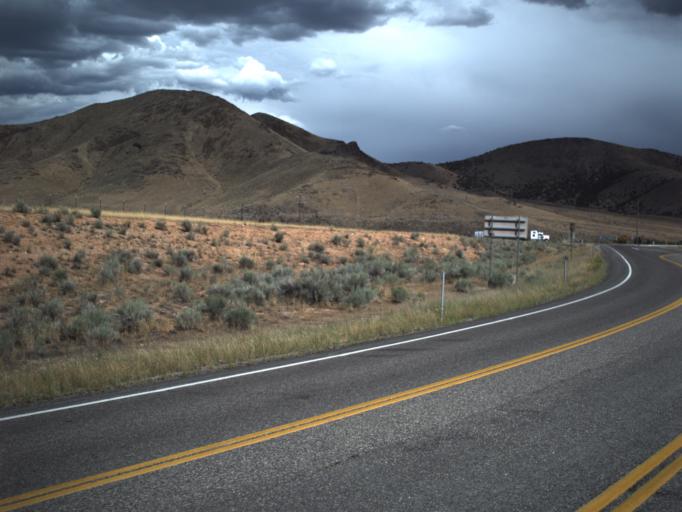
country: US
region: Utah
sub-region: Sevier County
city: Aurora
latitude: 38.8724
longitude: -111.9646
